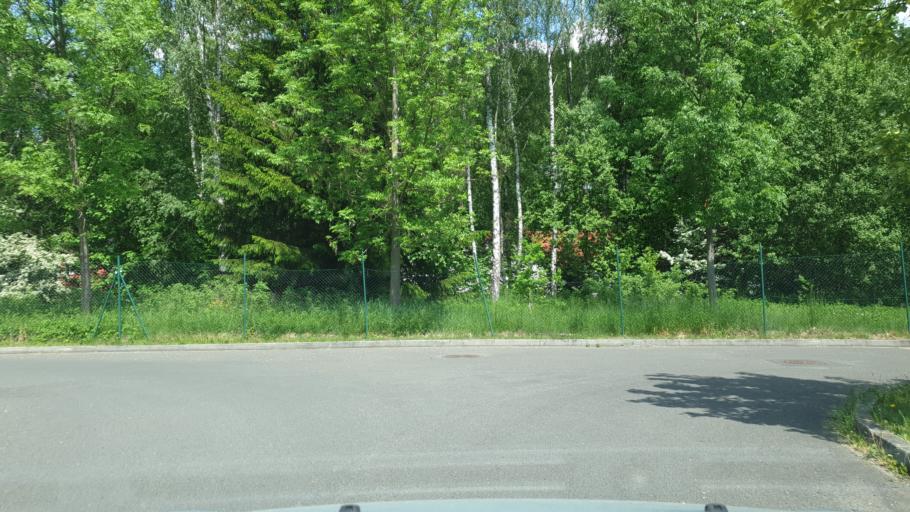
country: DE
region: Saxony
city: Klingenthal
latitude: 50.3532
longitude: 12.4710
